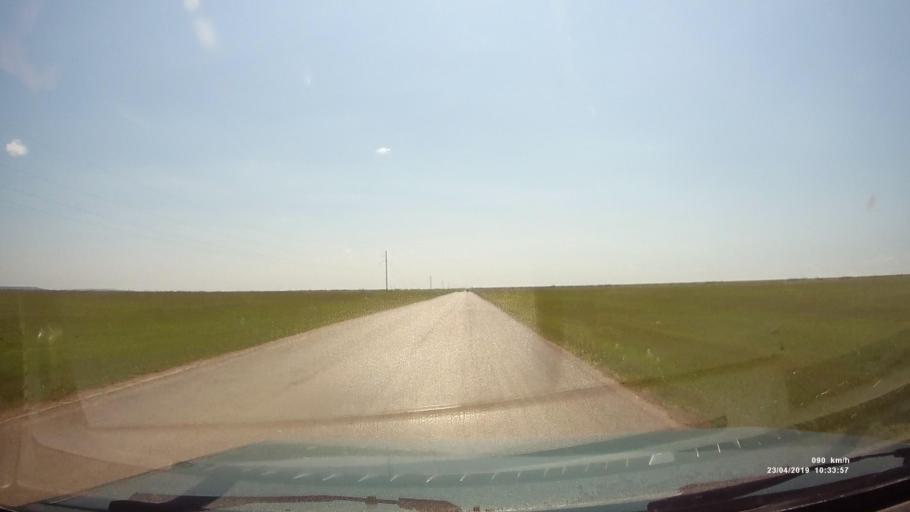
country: RU
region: Kalmykiya
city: Yashalta
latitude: 46.5687
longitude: 42.6040
